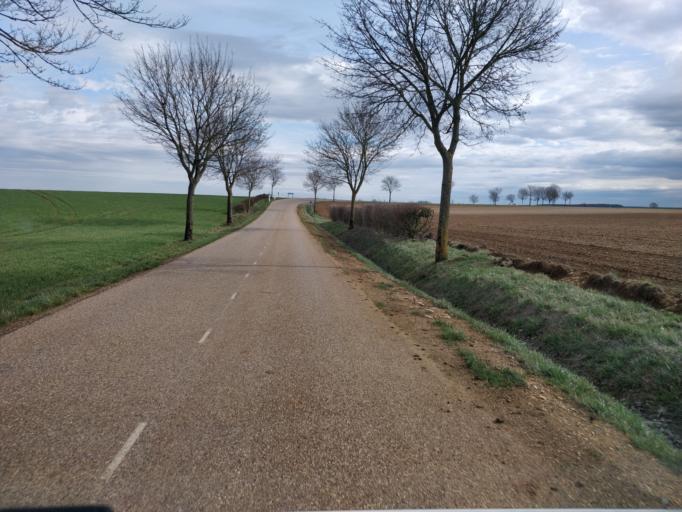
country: FR
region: Lorraine
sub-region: Departement de Meurthe-et-Moselle
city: Doncourt-les-Conflans
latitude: 49.1208
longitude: 5.9123
